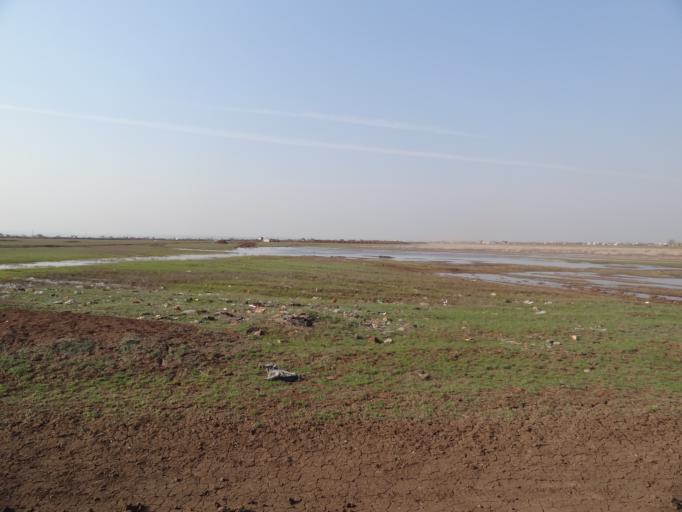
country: RU
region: Saratov
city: Privolzhskiy
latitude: 51.3221
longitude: 46.0040
